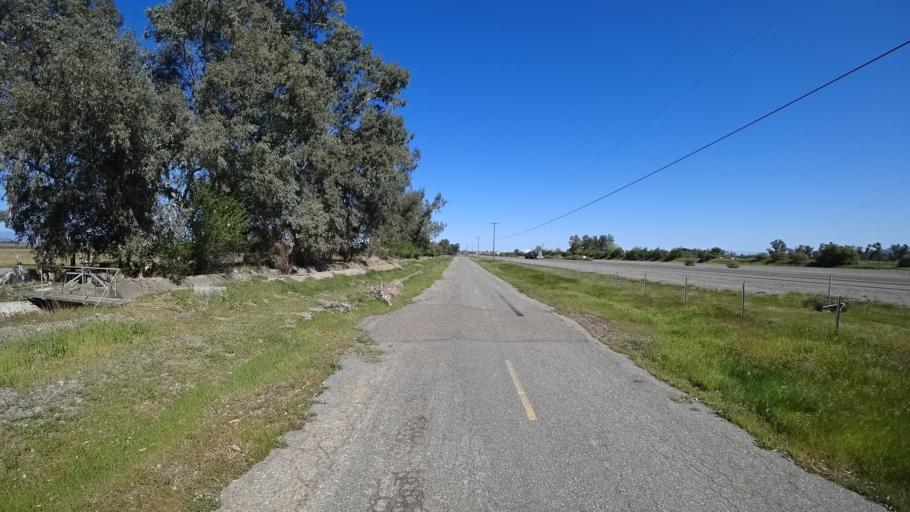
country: US
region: California
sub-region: Glenn County
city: Orland
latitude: 39.7043
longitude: -122.2064
